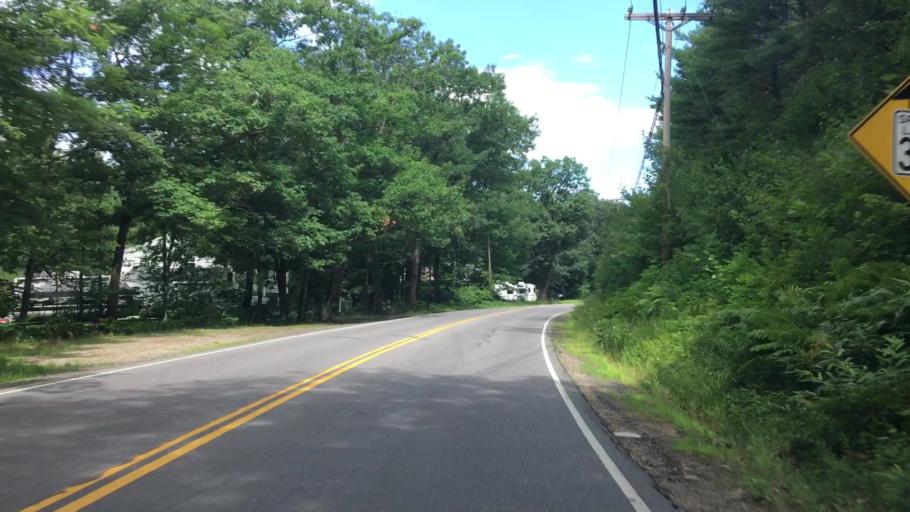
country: US
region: New Hampshire
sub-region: Belknap County
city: Meredith
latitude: 43.6070
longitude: -71.5243
